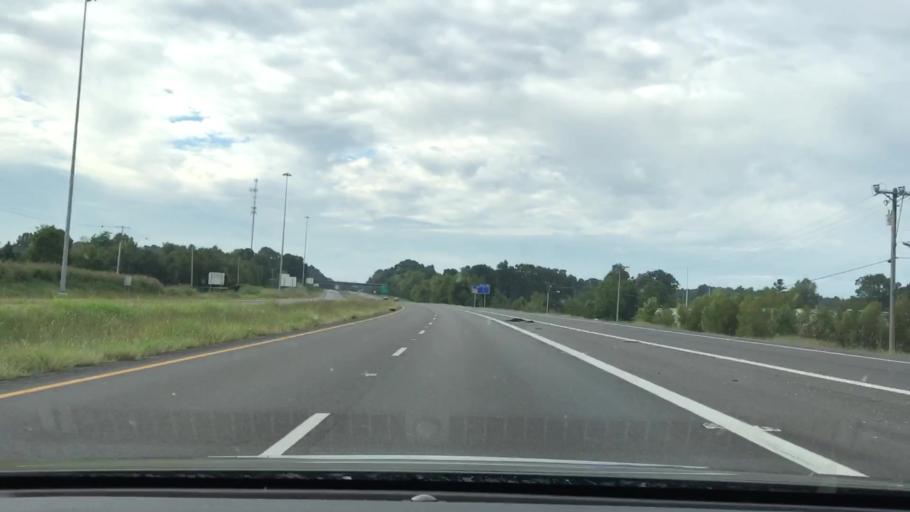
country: US
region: Kentucky
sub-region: Marshall County
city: Benton
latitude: 36.8665
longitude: -88.3664
